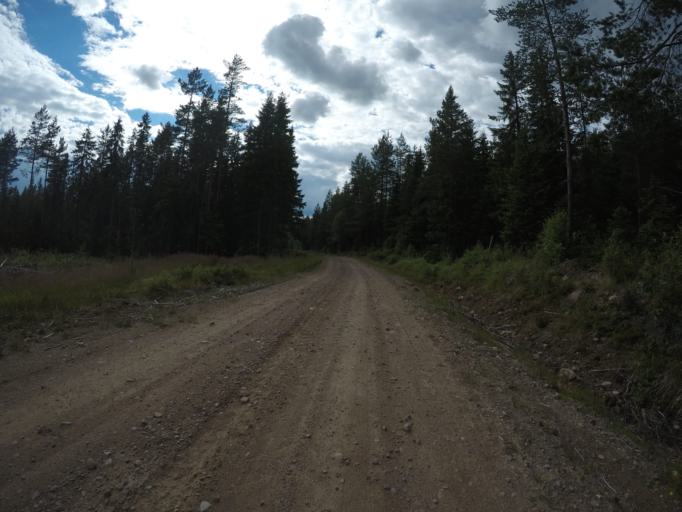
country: SE
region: Vaermland
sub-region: Filipstads Kommun
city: Lesjofors
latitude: 60.0823
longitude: 14.4297
